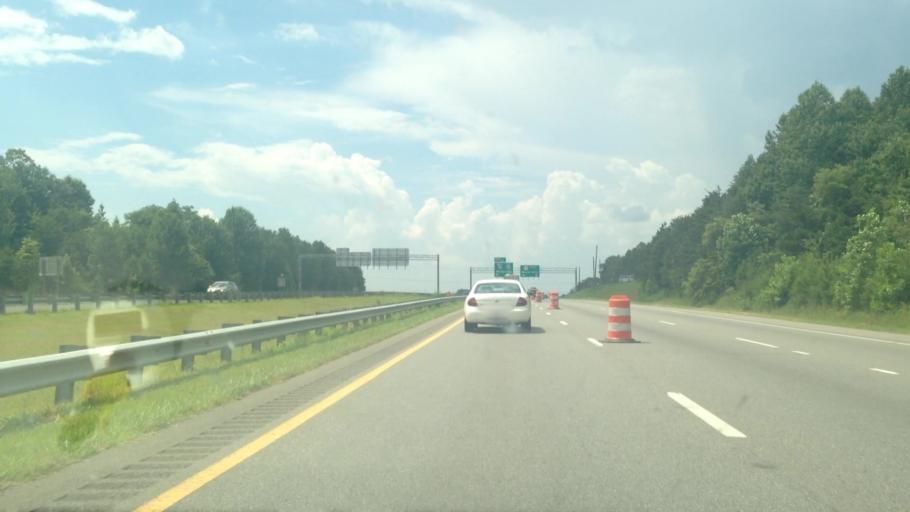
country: US
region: North Carolina
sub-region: Surry County
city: Flat Rock
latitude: 36.4440
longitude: -80.5422
